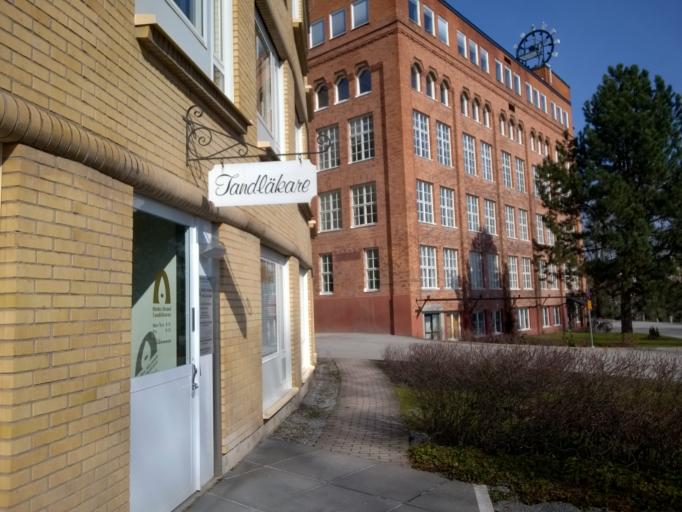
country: SE
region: Stockholm
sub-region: Solna Kommun
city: Solna
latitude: 59.3287
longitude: 17.9850
